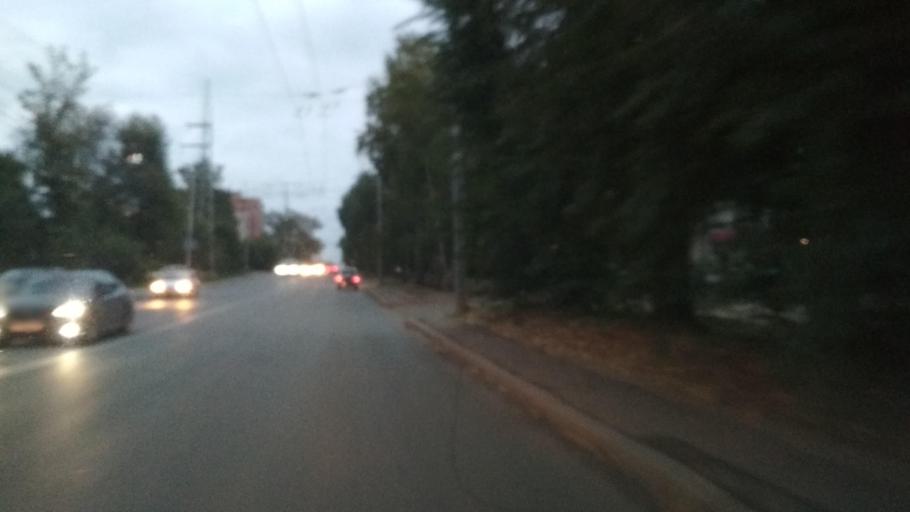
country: RU
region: Tomsk
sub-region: Tomskiy Rayon
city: Tomsk
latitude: 56.4761
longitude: 84.9925
